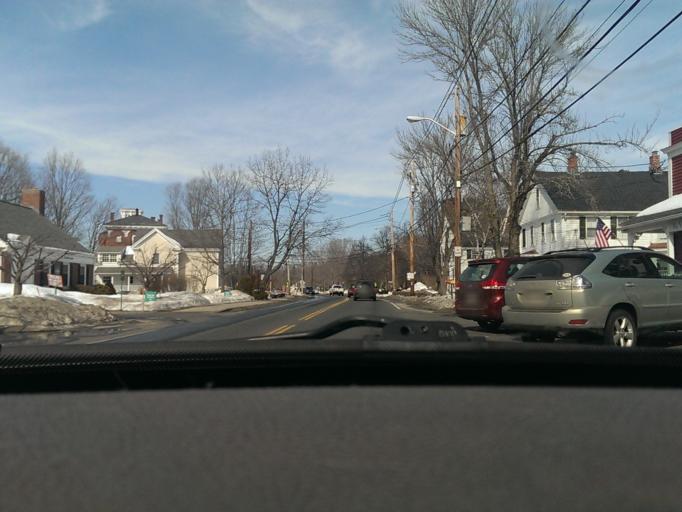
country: US
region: Massachusetts
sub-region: Hampden County
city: Wilbraham
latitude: 42.1223
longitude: -72.4314
